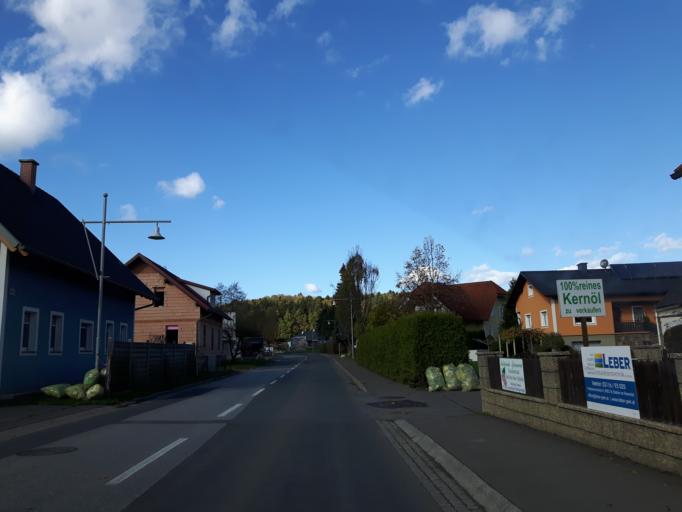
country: AT
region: Styria
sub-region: Politischer Bezirk Suedoststeiermark
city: Paldau
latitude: 46.9408
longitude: 15.7915
